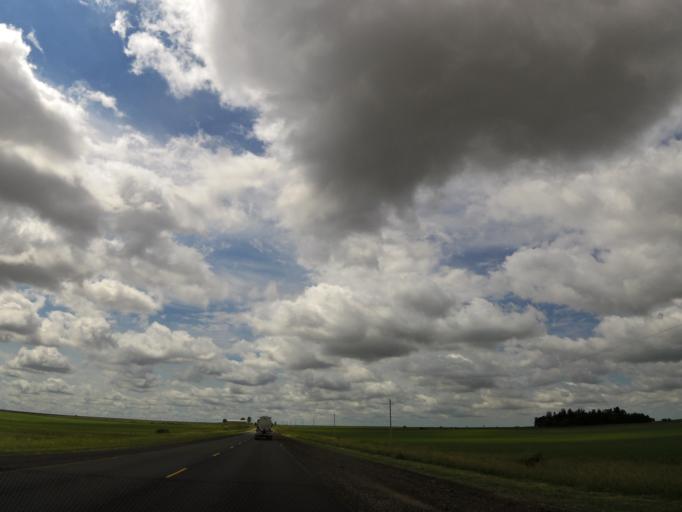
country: US
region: Iowa
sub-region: Howard County
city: Cresco
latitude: 43.3343
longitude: -92.2988
